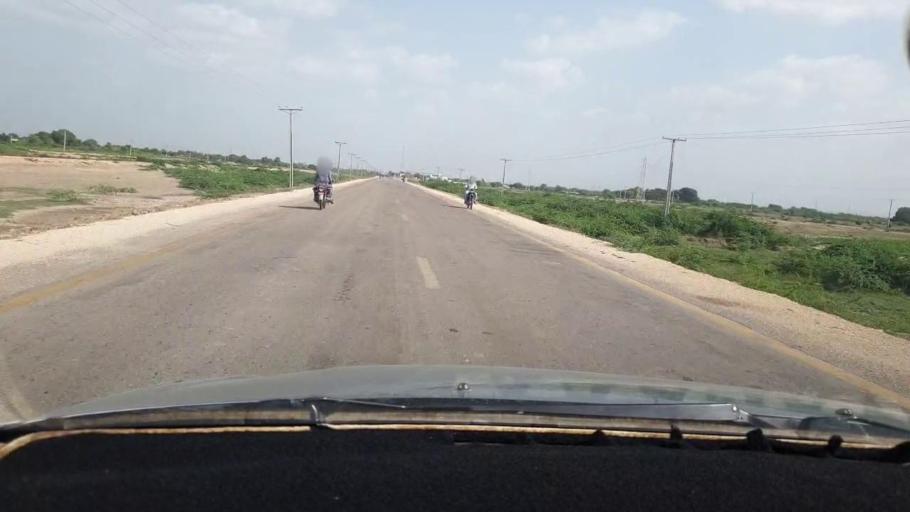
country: PK
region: Sindh
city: Naukot
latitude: 24.8714
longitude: 69.3743
